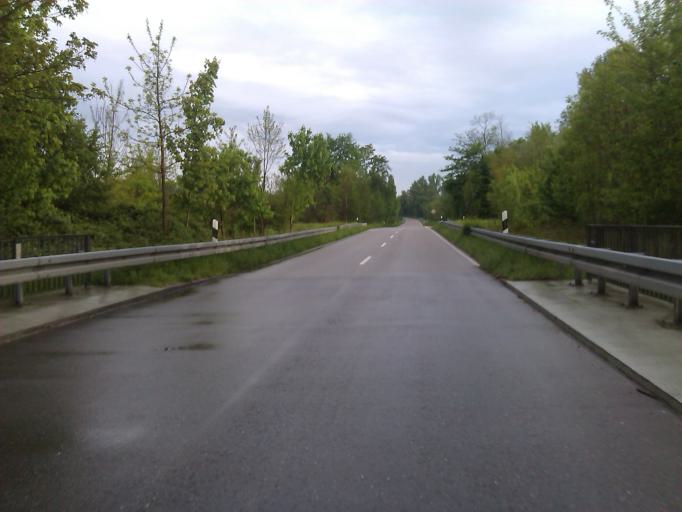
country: FR
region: Alsace
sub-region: Departement du Bas-Rhin
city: Drusenheim
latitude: 48.7459
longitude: 7.9734
